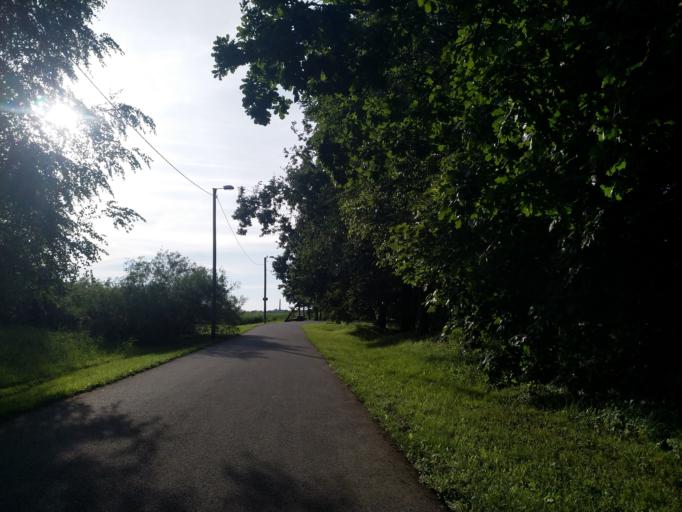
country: EE
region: Paernumaa
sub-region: Paernu linn
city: Parnu
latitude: 58.3834
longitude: 24.5370
